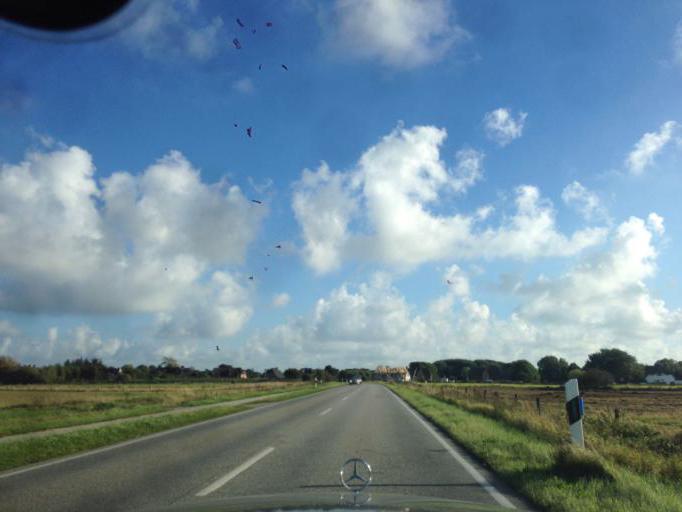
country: DE
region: Schleswig-Holstein
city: Sylt-Ost
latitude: 54.8766
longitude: 8.3917
